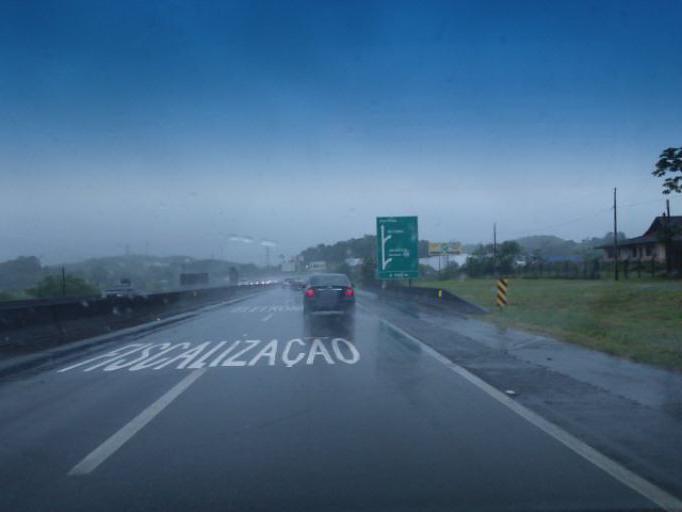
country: BR
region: Santa Catarina
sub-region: Joinville
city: Joinville
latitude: -26.3922
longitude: -48.8395
